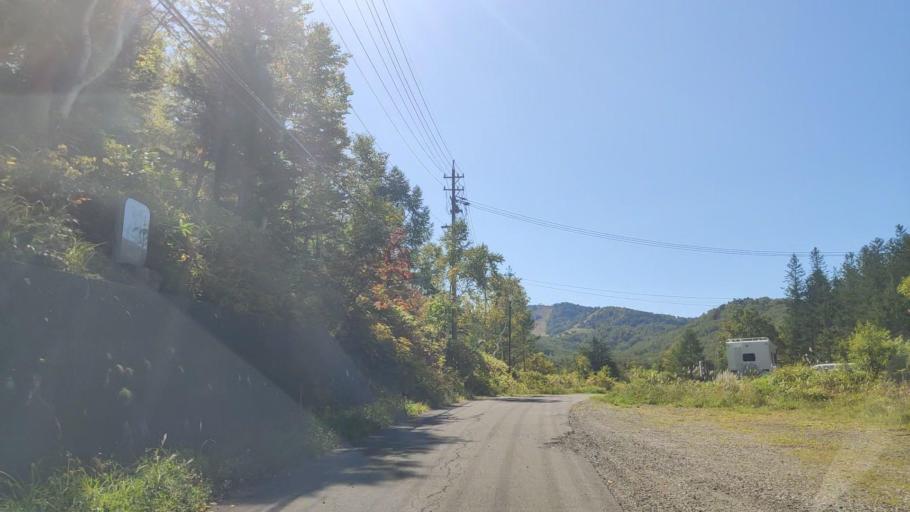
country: JP
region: Nagano
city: Nakano
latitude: 36.6966
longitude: 138.4893
